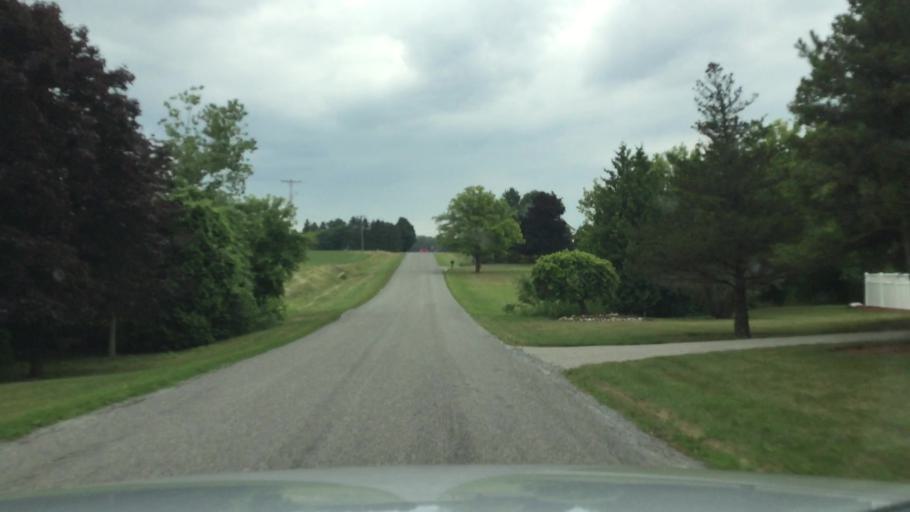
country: US
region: Michigan
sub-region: Saginaw County
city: Birch Run
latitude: 43.3117
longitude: -83.7956
